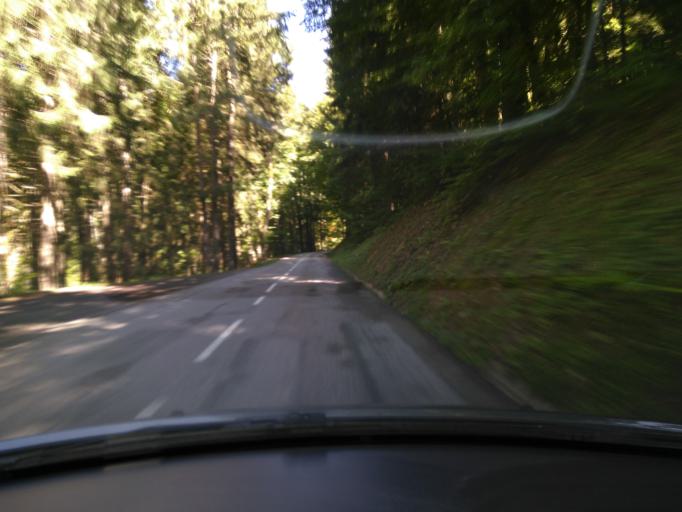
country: FR
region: Rhone-Alpes
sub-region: Departement de la Haute-Savoie
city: Praz-sur-Arly
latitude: 45.7963
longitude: 6.4935
